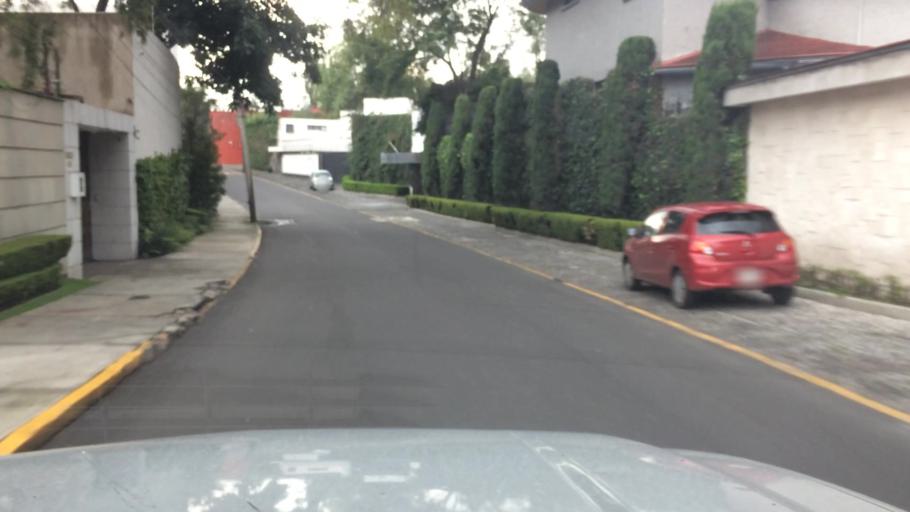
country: MX
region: Mexico City
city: Magdalena Contreras
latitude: 19.3252
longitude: -99.2088
